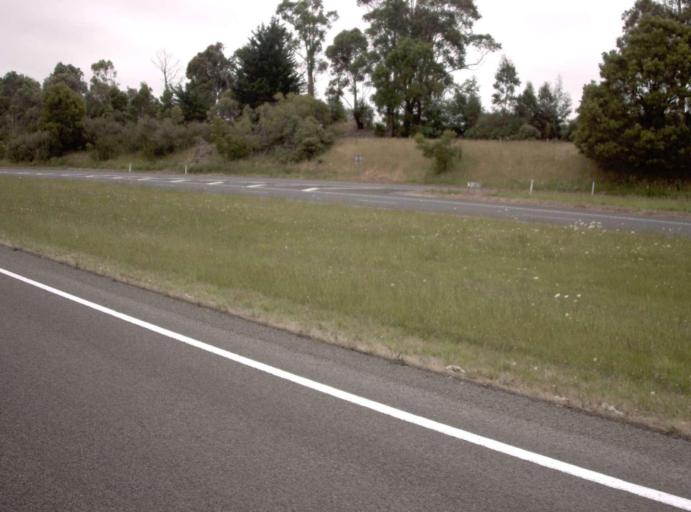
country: AU
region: Victoria
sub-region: Baw Baw
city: Warragul
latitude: -38.1382
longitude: 145.8829
